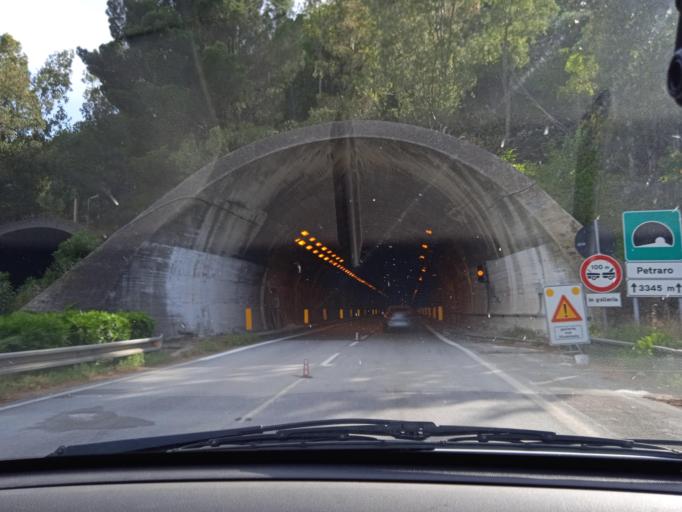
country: IT
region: Sicily
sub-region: Messina
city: Gioiosa Marea
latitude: 38.1575
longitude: 14.9038
